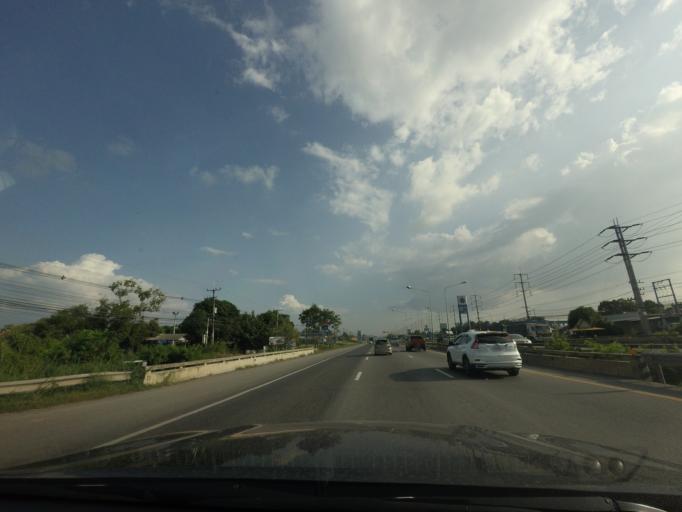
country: TH
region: Sara Buri
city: Chaloem Phra Kiat
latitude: 14.5769
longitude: 100.9015
